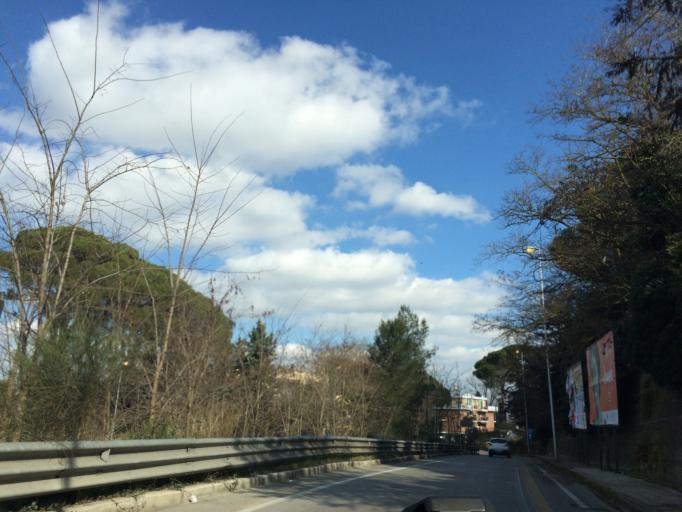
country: IT
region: Basilicate
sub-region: Provincia di Matera
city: Matera
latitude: 40.6609
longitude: 16.5956
